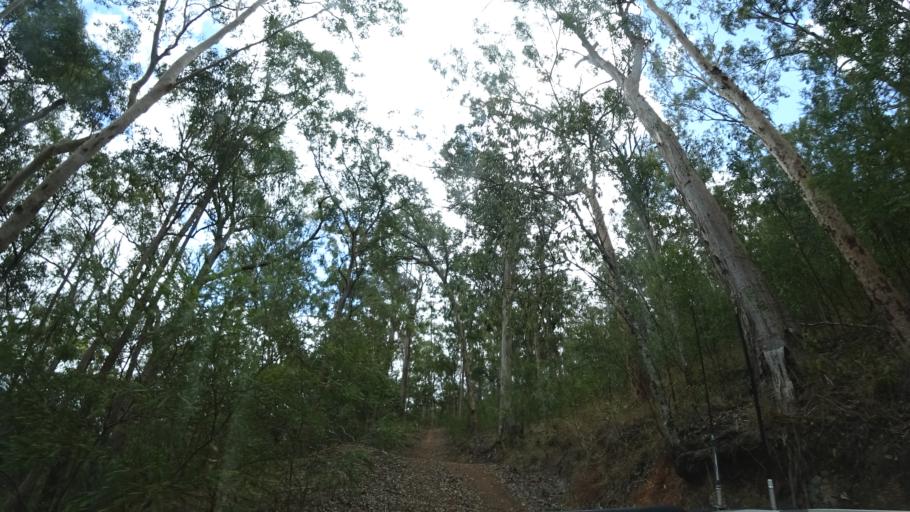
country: AU
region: Queensland
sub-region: Moreton Bay
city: Highvale
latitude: -27.4081
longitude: 152.7401
